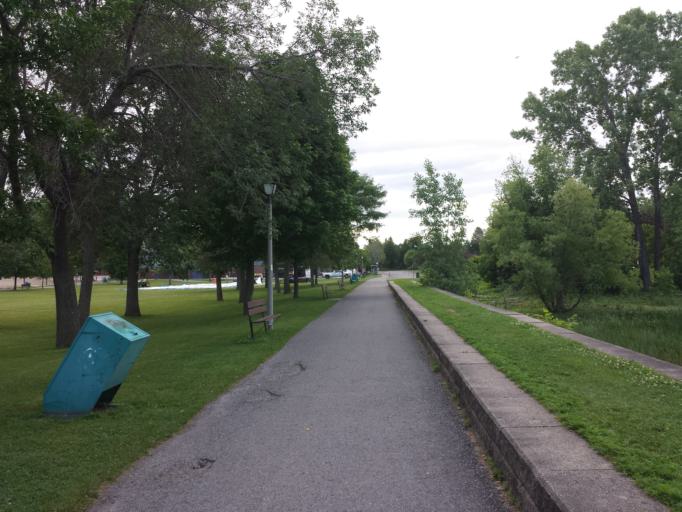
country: CA
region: Ontario
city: Bells Corners
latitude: 45.3642
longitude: -75.8043
